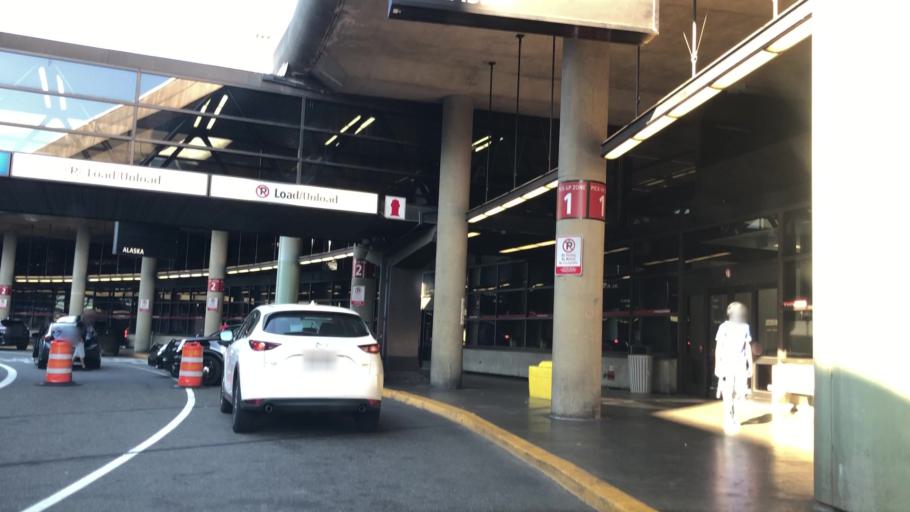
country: US
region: Washington
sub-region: King County
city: SeaTac
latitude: 47.4441
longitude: -122.3014
